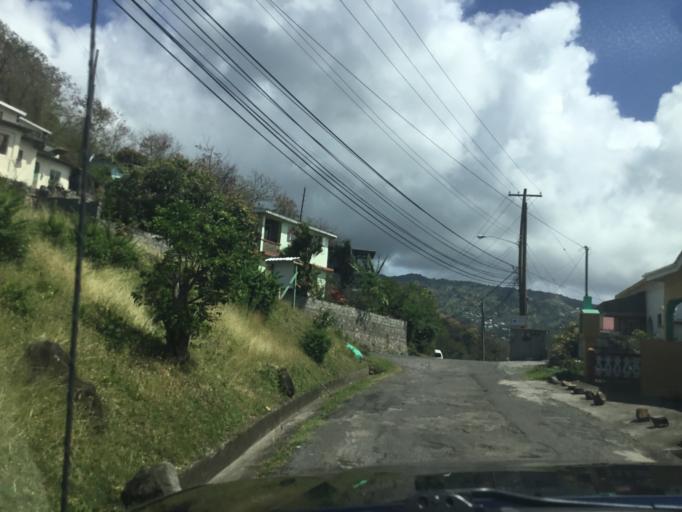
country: VC
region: Saint George
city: Kingstown Park
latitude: 13.1604
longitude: -61.2385
